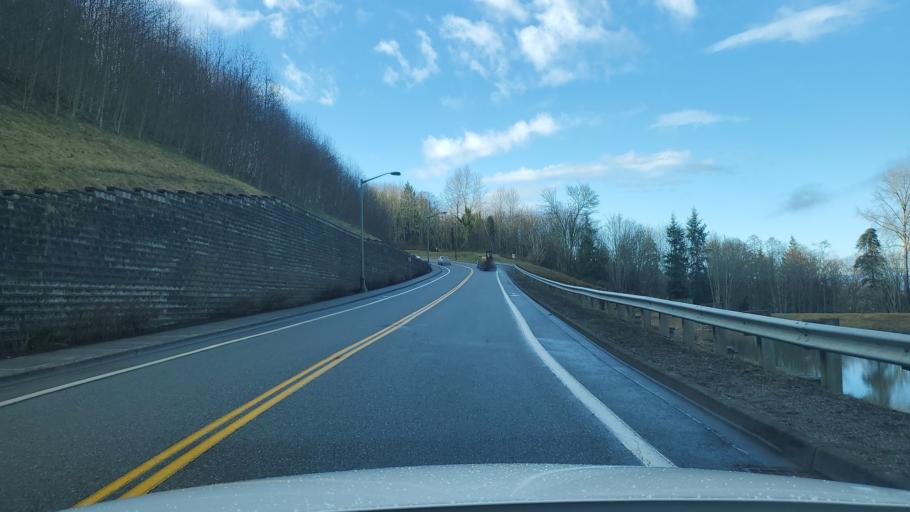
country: US
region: Washington
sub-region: Skagit County
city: Big Lake
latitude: 48.4290
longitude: -122.2708
